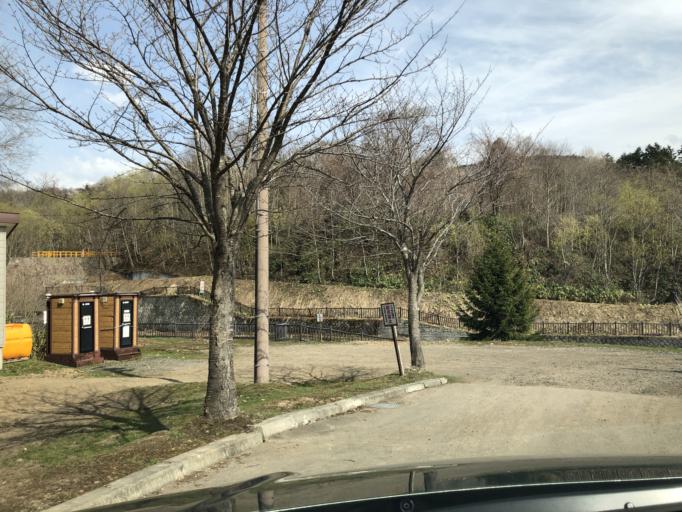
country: JP
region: Hokkaido
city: Akabira
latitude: 43.5943
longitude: 142.0482
